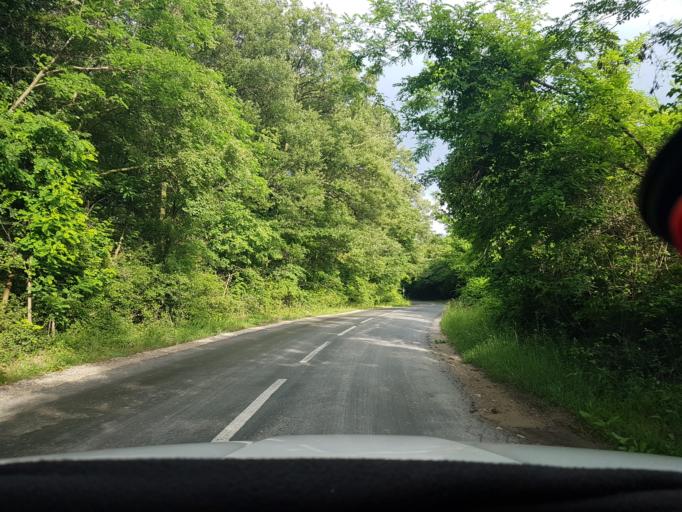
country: HU
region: Komarom-Esztergom
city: Nyergesujfalu
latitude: 47.7255
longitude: 18.5377
